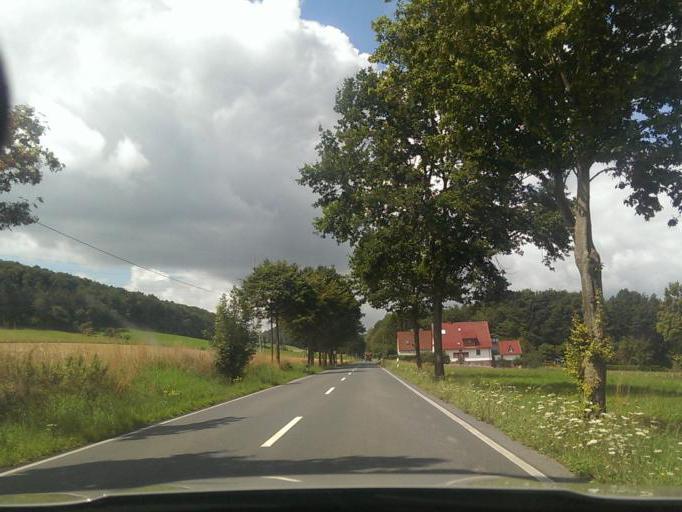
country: DE
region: North Rhine-Westphalia
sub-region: Regierungsbezirk Detmold
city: Hoexter
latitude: 51.8196
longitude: 9.3935
